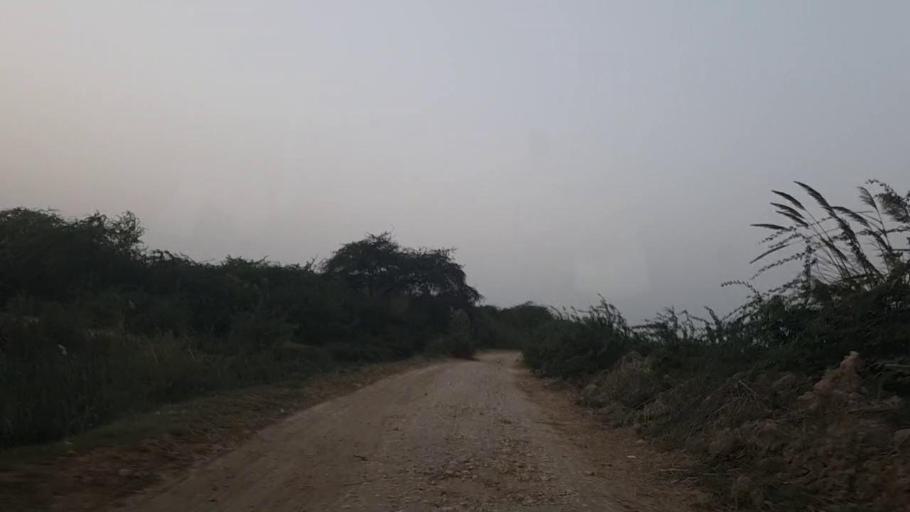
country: PK
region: Sindh
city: Mirpur Sakro
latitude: 24.5759
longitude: 67.7868
